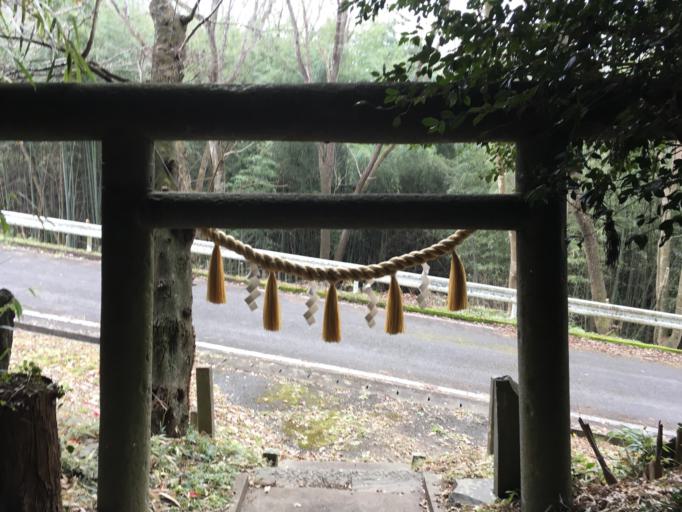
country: JP
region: Miyagi
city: Wakuya
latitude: 38.6816
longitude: 141.2767
